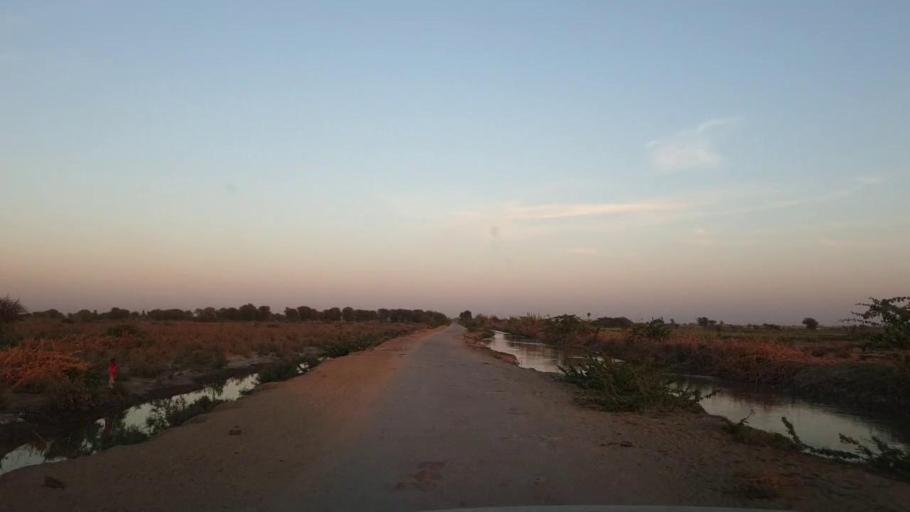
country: PK
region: Sindh
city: Samaro
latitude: 25.1482
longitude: 69.4270
